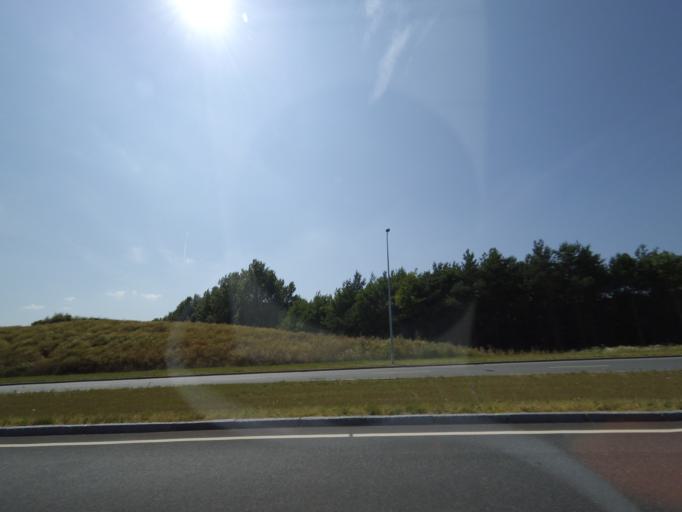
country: DK
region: South Denmark
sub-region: Odense Kommune
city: Hojby
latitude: 55.3543
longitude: 10.4218
